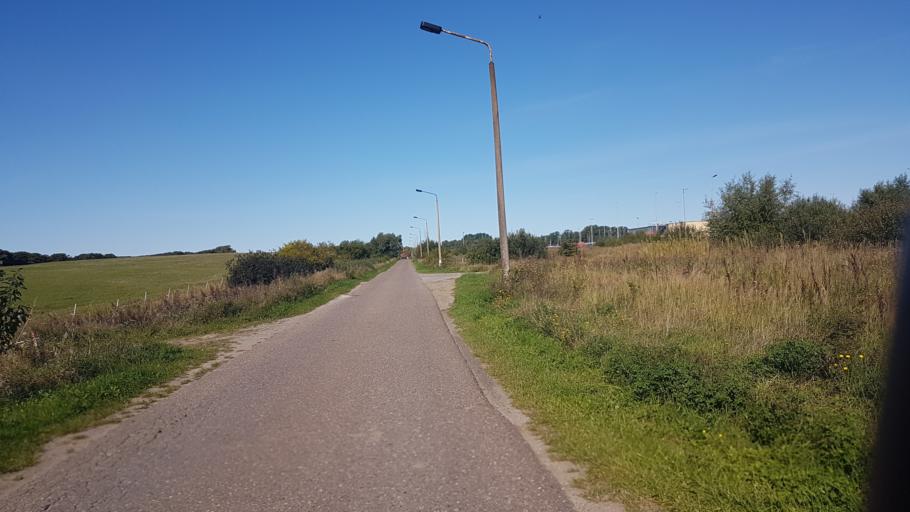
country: DE
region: Mecklenburg-Vorpommern
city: Sagard
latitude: 54.4970
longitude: 13.5473
